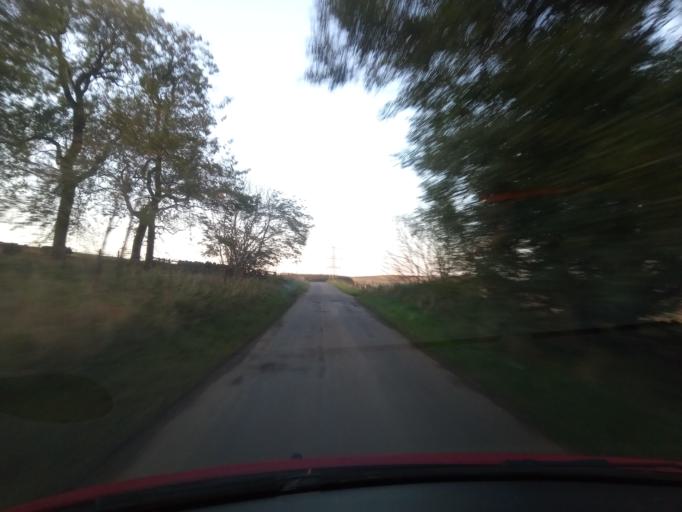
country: GB
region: Scotland
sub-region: East Lothian
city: Pencaitland
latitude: 55.8002
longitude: -2.8880
